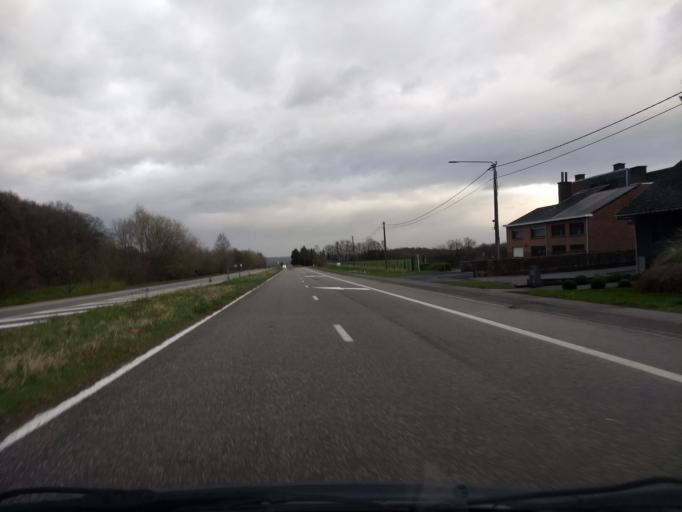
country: BE
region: Wallonia
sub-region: Province du Hainaut
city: Ellezelles
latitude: 50.7708
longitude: 3.7035
